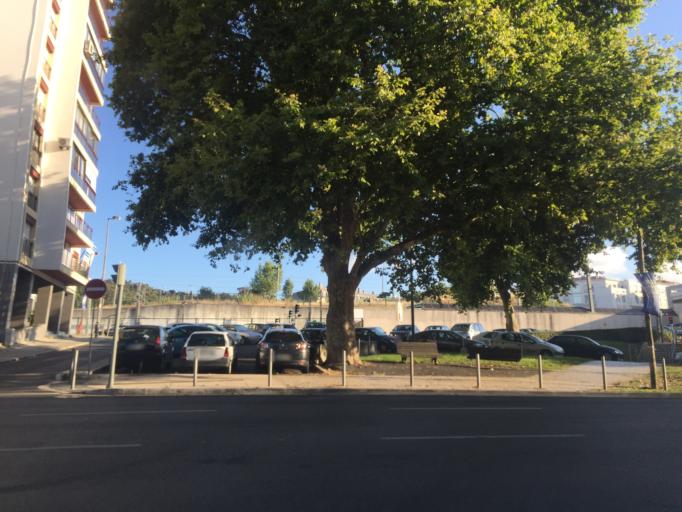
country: PT
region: Lisbon
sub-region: Odivelas
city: Pontinha
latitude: 38.7450
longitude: -9.1981
